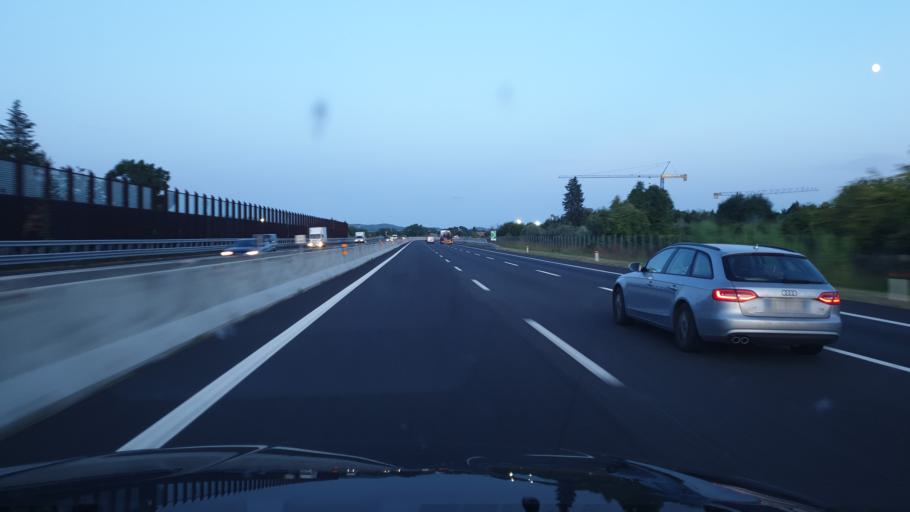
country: IT
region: Emilia-Romagna
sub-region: Provincia di Rimini
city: Santa Monica-Cella
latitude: 43.9687
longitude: 12.6787
